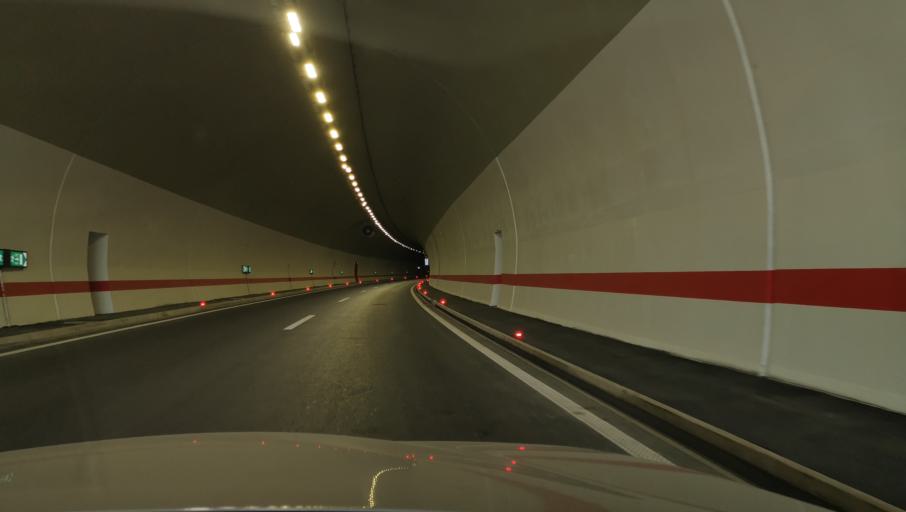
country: RS
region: Central Serbia
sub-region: Kolubarski Okrug
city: Ljig
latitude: 44.2110
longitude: 20.2629
